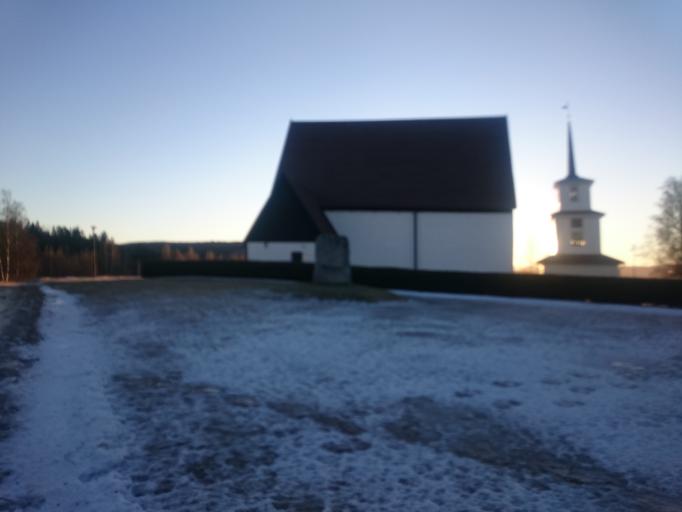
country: SE
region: Vaesternorrland
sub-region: OErnskoeldsviks Kommun
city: Bjasta
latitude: 63.2915
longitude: 18.2948
